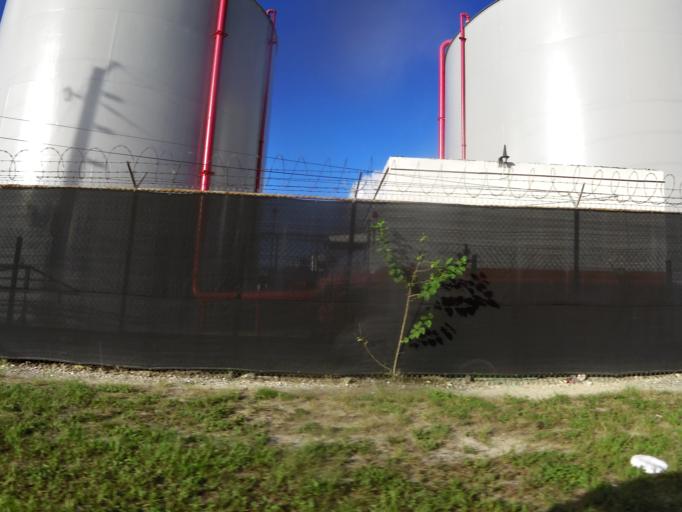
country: US
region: Florida
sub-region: Duval County
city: Jacksonville
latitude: 30.3788
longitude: -81.6653
